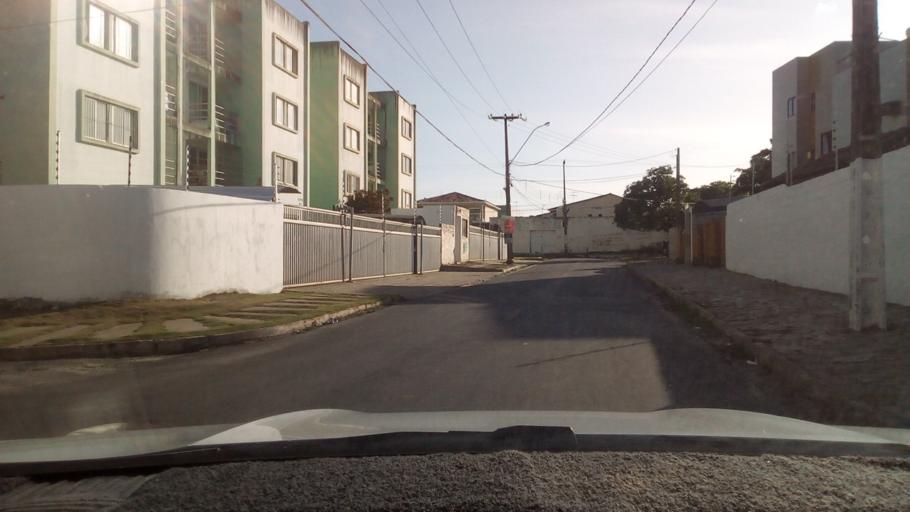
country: BR
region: Paraiba
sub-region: Joao Pessoa
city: Joao Pessoa
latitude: -7.1716
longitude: -34.8591
